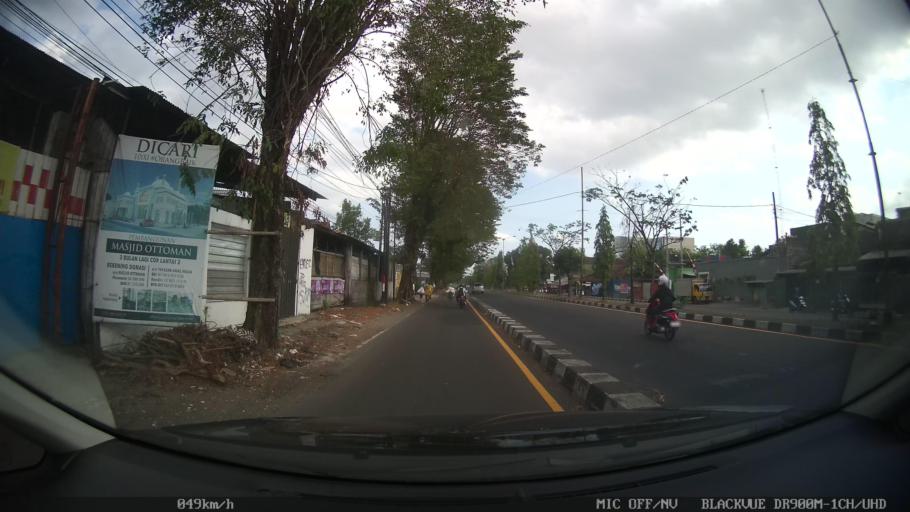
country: ID
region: Daerah Istimewa Yogyakarta
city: Gamping Lor
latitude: -7.7671
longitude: 110.3351
